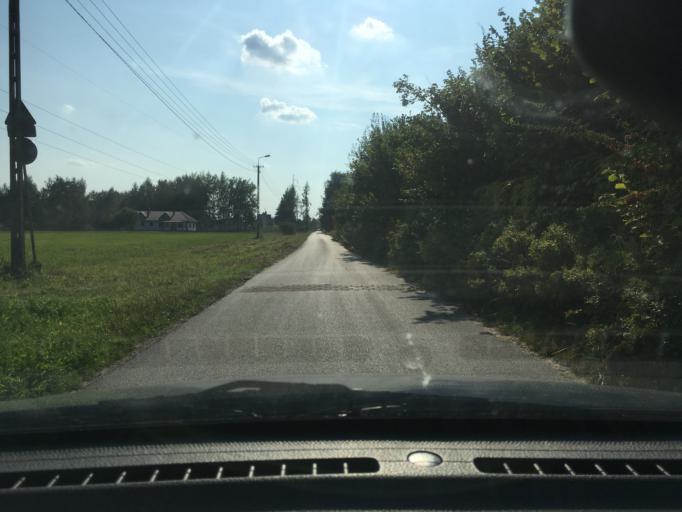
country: PL
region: Masovian Voivodeship
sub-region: Powiat piaseczynski
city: Lesznowola
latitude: 52.0526
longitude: 20.9431
